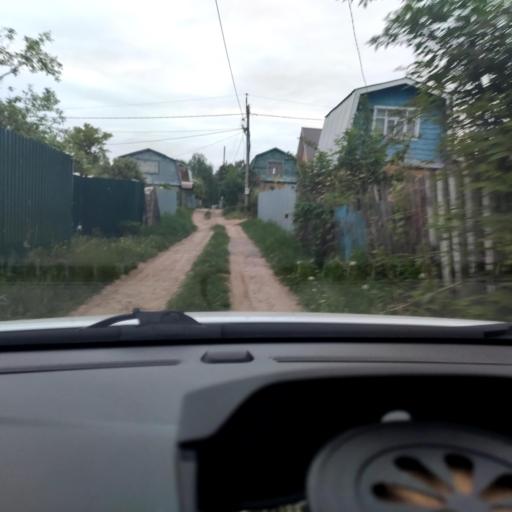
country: RU
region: Tatarstan
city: Vysokaya Gora
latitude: 55.8526
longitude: 49.2492
